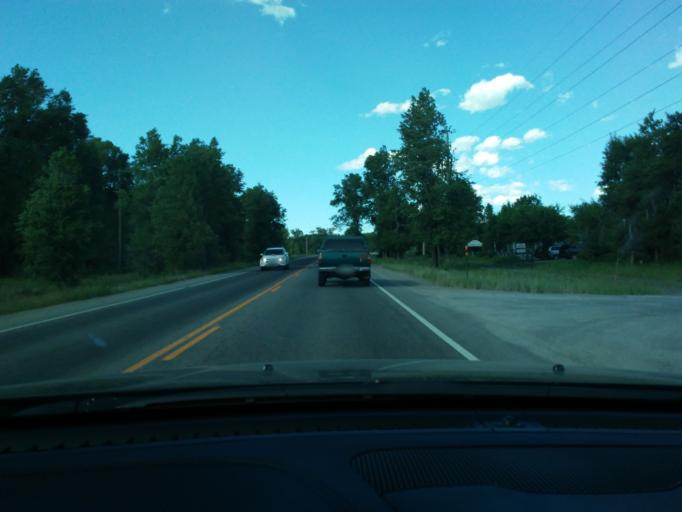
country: US
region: Wyoming
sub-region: Teton County
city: Moose Wilson Road
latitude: 43.5325
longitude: -110.8391
